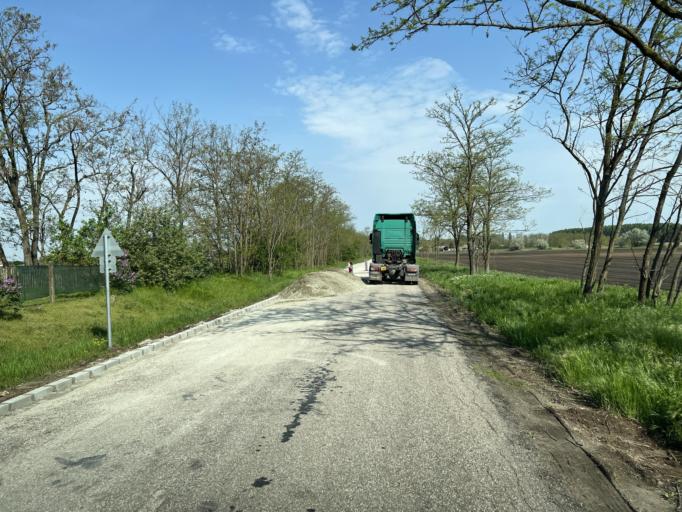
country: HU
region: Pest
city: Kocser
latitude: 46.9832
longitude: 19.9821
